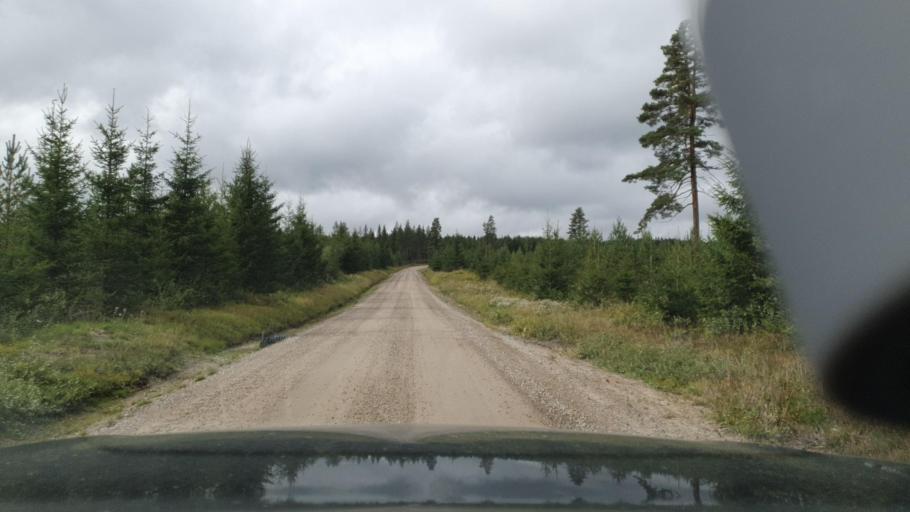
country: NO
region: Hedmark
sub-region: Trysil
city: Innbygda
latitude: 60.9415
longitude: 12.4490
